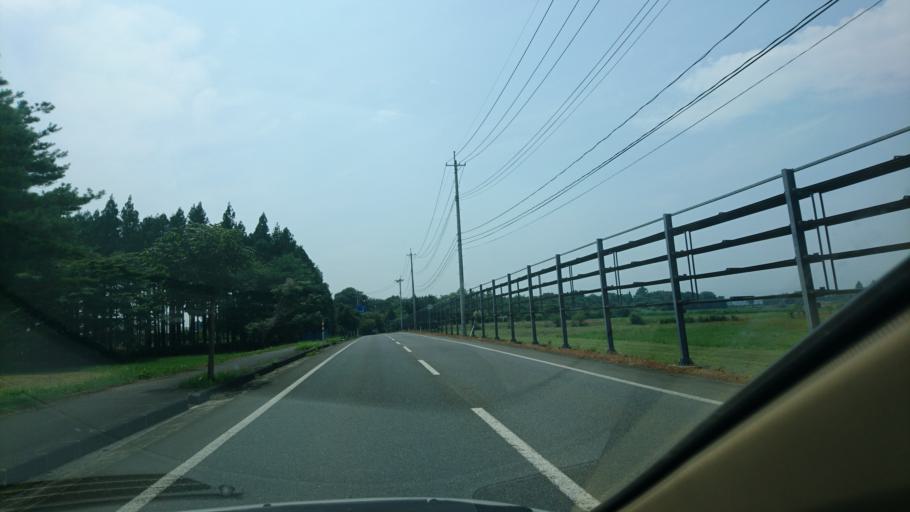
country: JP
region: Iwate
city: Kitakami
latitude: 39.2589
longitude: 141.0843
